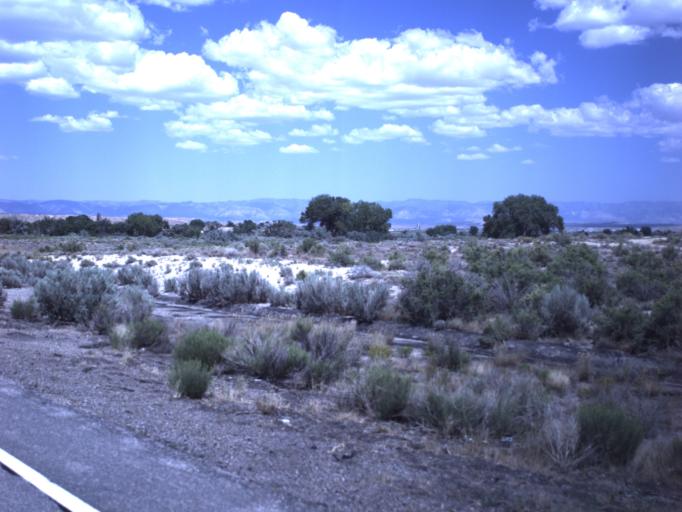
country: US
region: Utah
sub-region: Carbon County
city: Price
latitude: 39.5182
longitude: -110.8279
